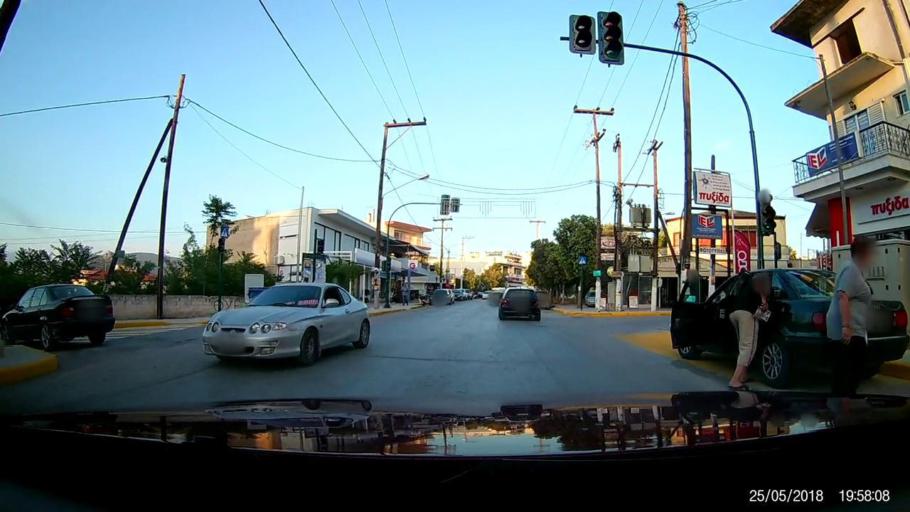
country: GR
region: Central Greece
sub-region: Nomos Evvoias
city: Vasilikon
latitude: 38.4259
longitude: 23.6705
